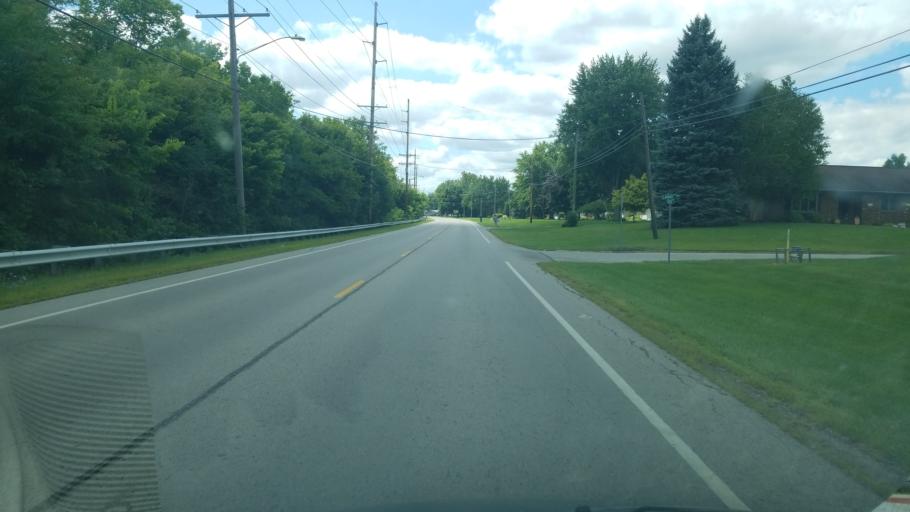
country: US
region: Ohio
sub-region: Henry County
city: Napoleon
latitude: 41.4083
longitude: -84.1003
